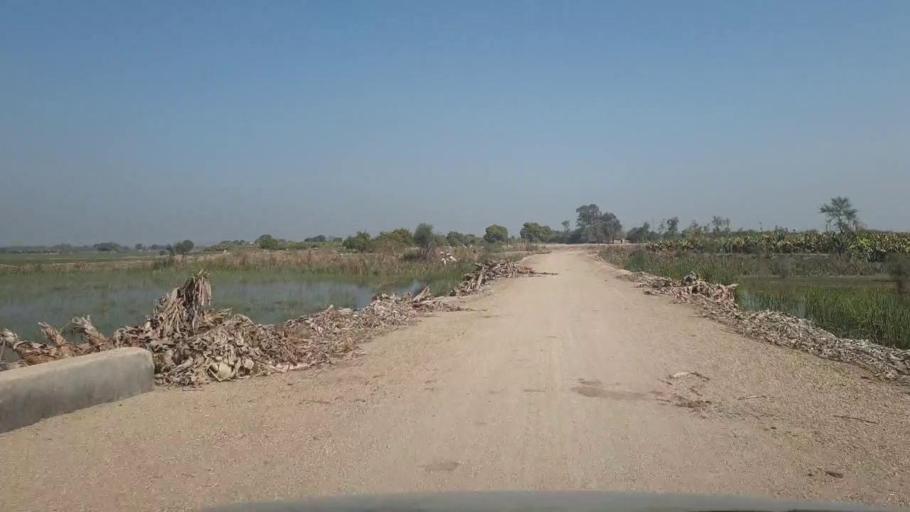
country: PK
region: Sindh
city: Chambar
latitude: 25.3745
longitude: 68.7862
